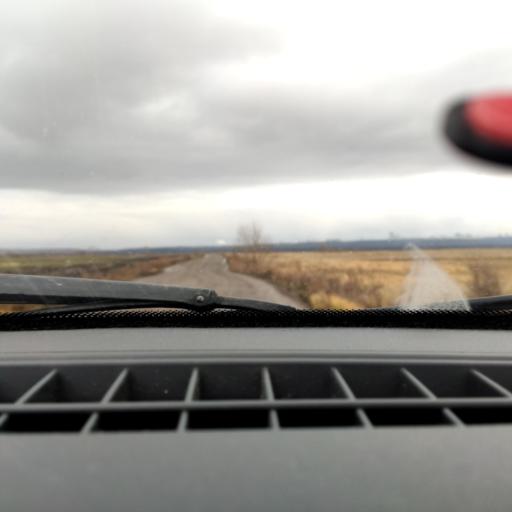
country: RU
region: Bashkortostan
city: Mikhaylovka
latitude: 54.8096
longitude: 55.9498
